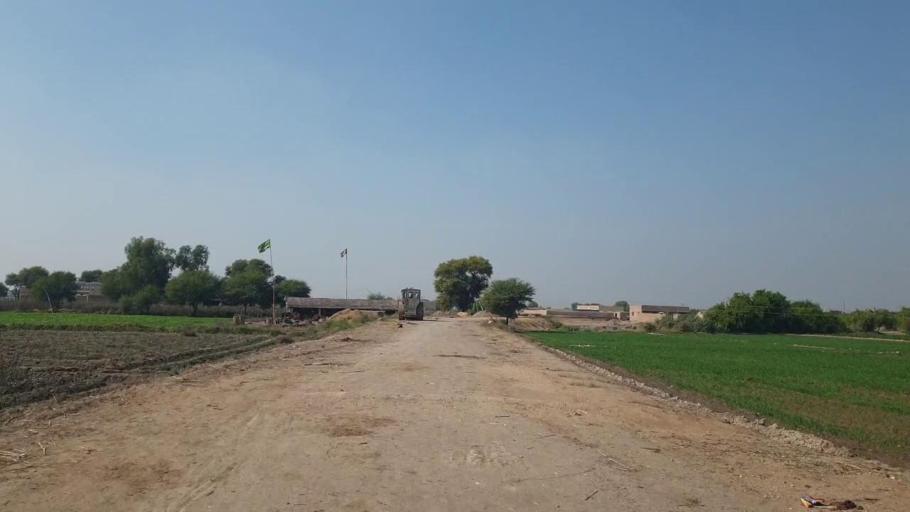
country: PK
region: Sindh
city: Sehwan
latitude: 26.4295
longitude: 67.8186
